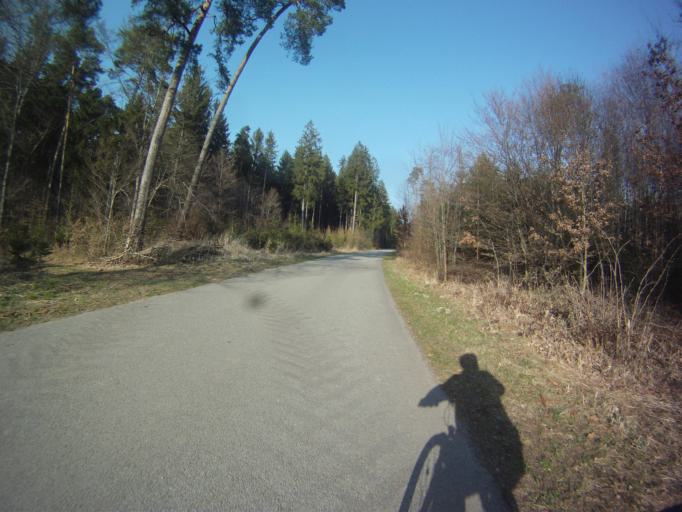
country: DE
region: Bavaria
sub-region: Upper Bavaria
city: Haiming
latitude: 48.2268
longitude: 12.8850
